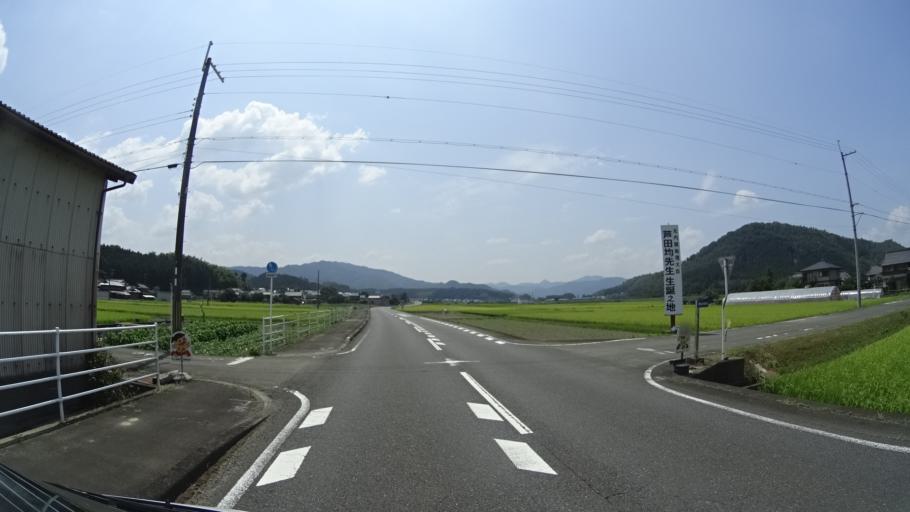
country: JP
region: Kyoto
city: Fukuchiyama
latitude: 35.2597
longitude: 135.1802
